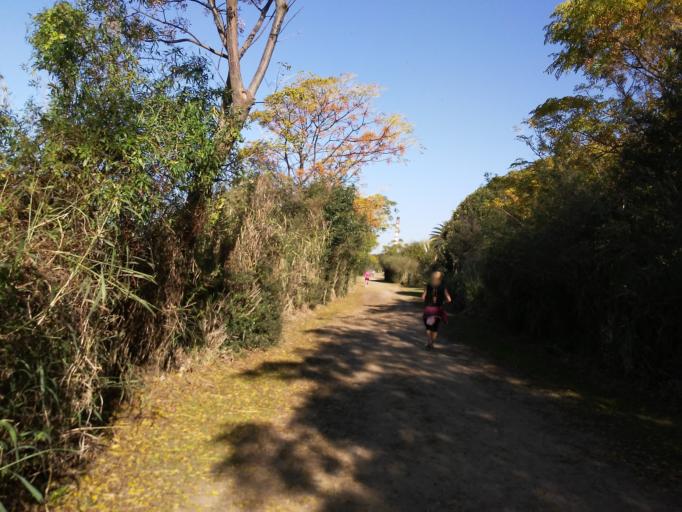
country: AR
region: Buenos Aires F.D.
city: Buenos Aires
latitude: -34.6120
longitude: -58.3408
